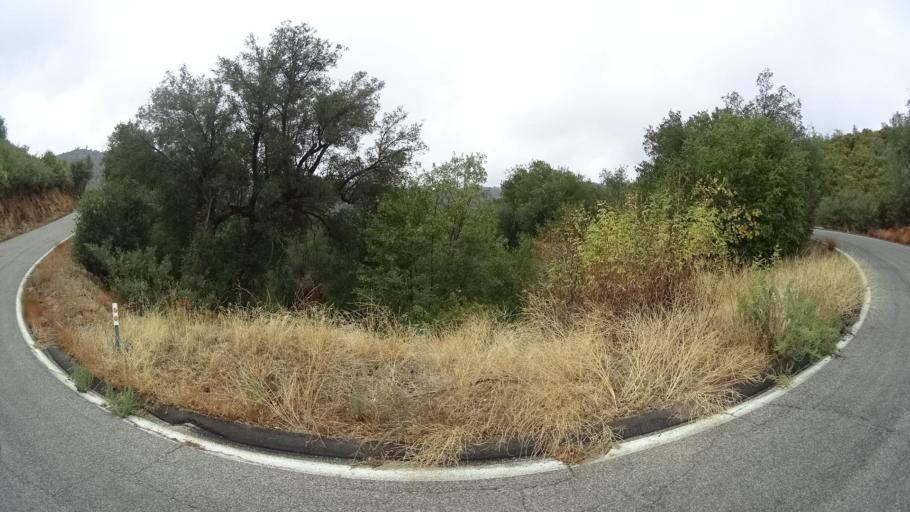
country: US
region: California
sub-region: San Diego County
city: Julian
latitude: 33.0174
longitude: -116.6312
